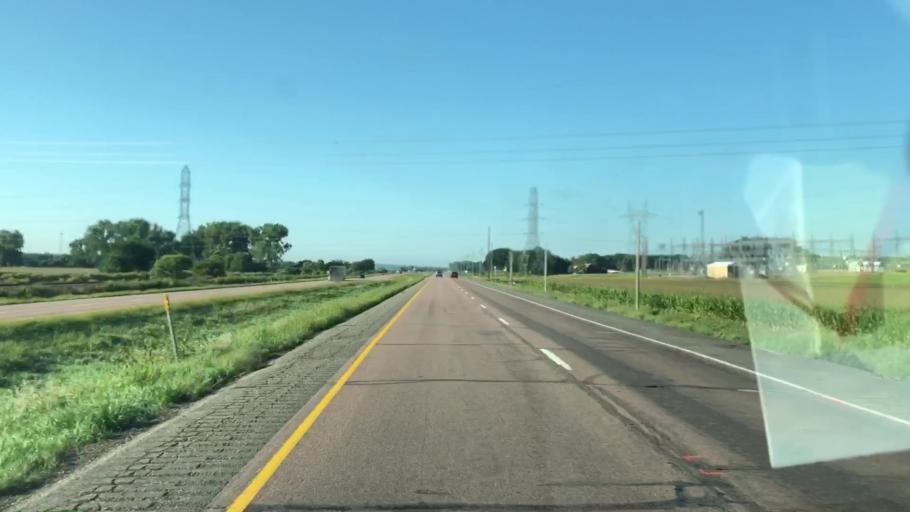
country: US
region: Iowa
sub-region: Woodbury County
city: Sioux City
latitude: 42.6033
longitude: -96.3007
